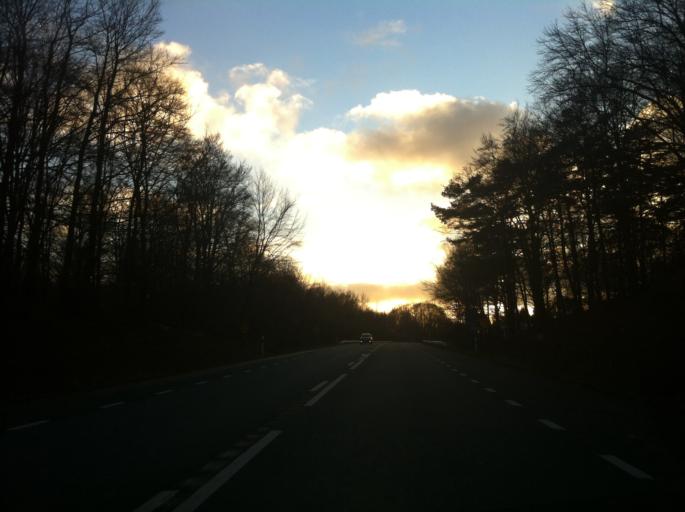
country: SE
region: Skane
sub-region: Hassleholms Kommun
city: Sosdala
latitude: 56.0251
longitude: 13.6751
